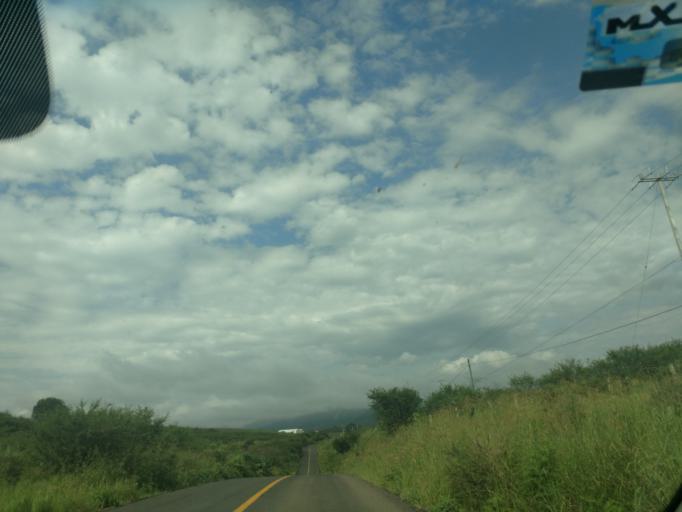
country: MX
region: Jalisco
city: El Salto
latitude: 20.4295
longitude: -104.4903
